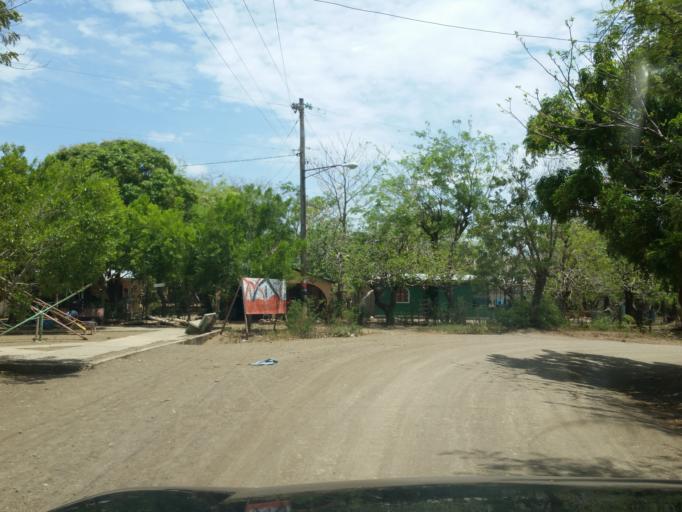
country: NI
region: Rivas
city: Tola
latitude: 11.5213
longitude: -86.0713
